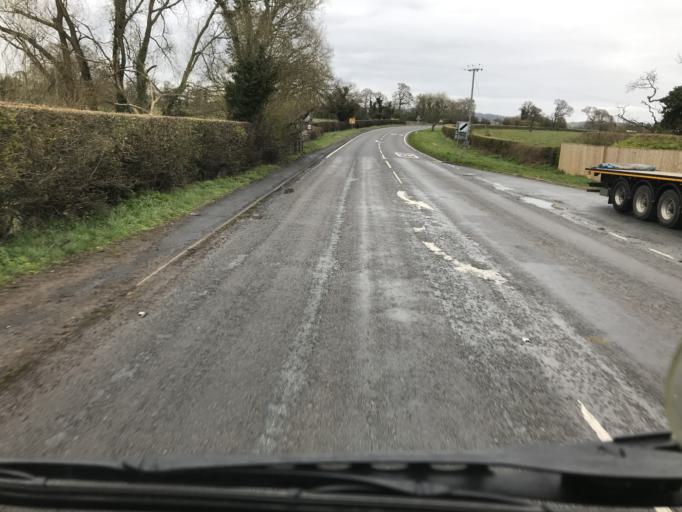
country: GB
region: England
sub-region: Cheshire West and Chester
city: Tattenhall
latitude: 53.1204
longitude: -2.8039
